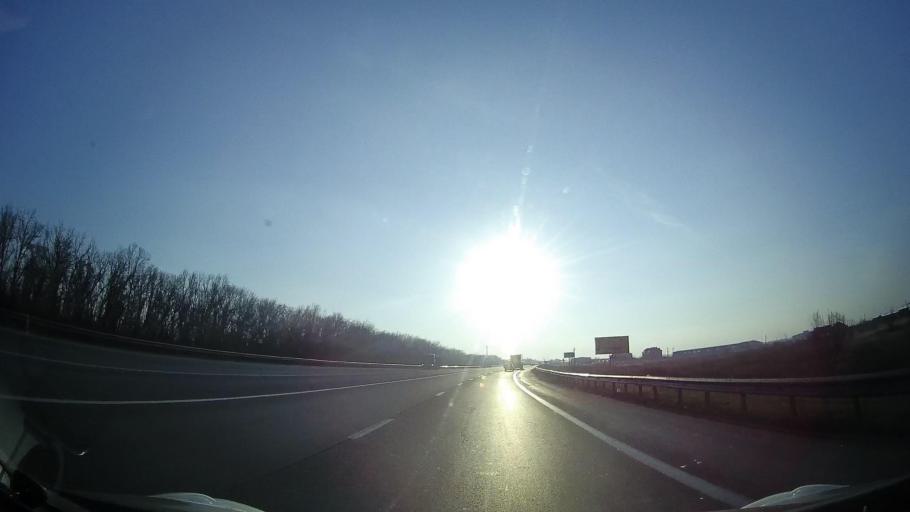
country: RU
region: Rostov
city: Ol'ginskaya
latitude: 47.1257
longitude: 39.8726
